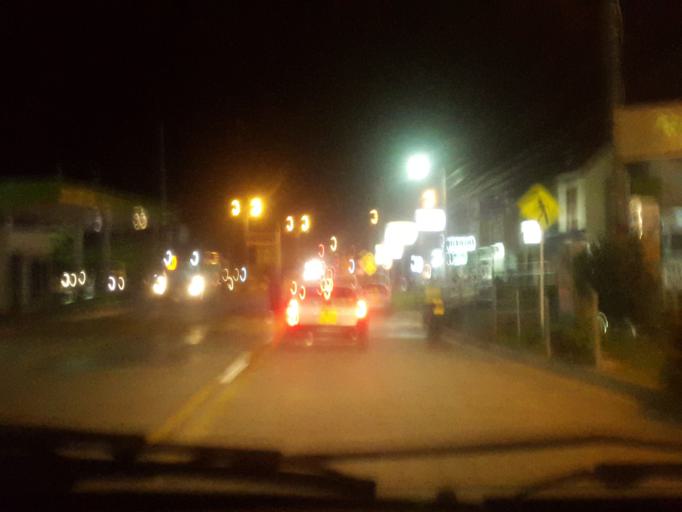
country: CO
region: Quindio
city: Armenia
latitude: 4.5206
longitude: -75.6985
